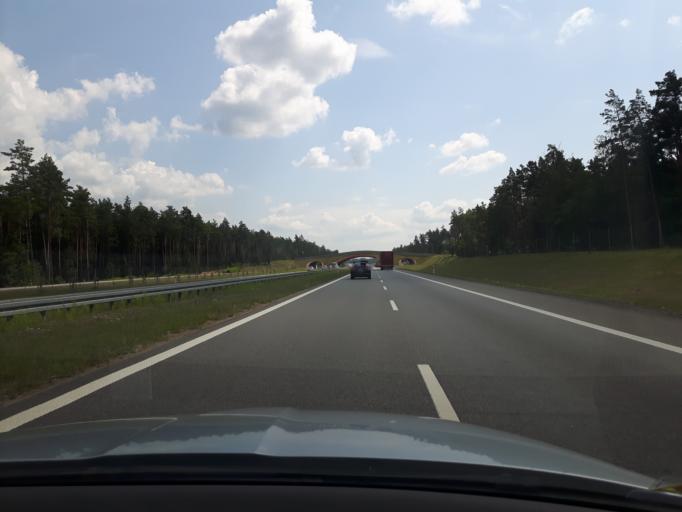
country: PL
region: Warmian-Masurian Voivodeship
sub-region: Powiat ostrodzki
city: Milomlyn
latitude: 53.7541
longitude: 19.8703
